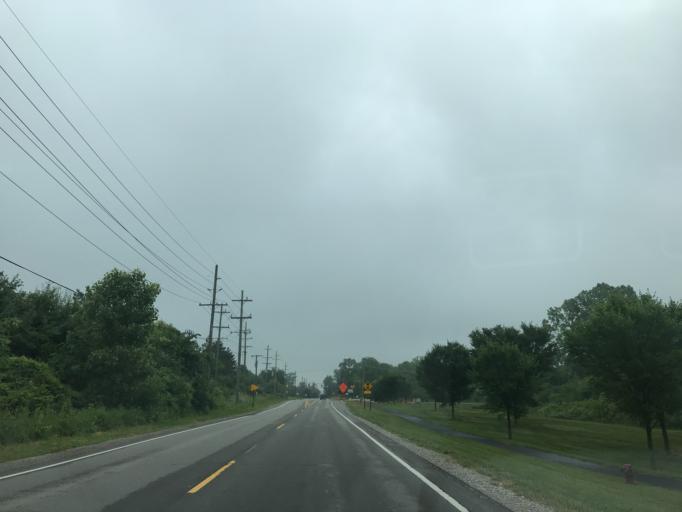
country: US
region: Michigan
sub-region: Washtenaw County
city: Ypsilanti
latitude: 42.2748
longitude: -83.6262
